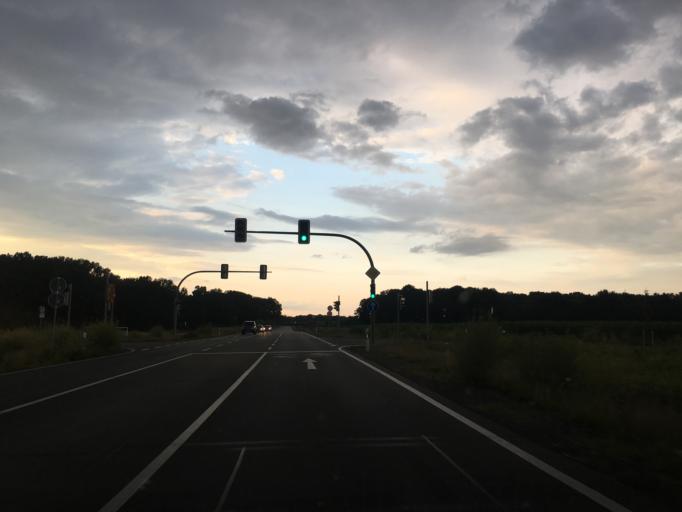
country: DE
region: North Rhine-Westphalia
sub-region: Regierungsbezirk Munster
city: Telgte
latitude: 51.9203
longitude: 7.7134
